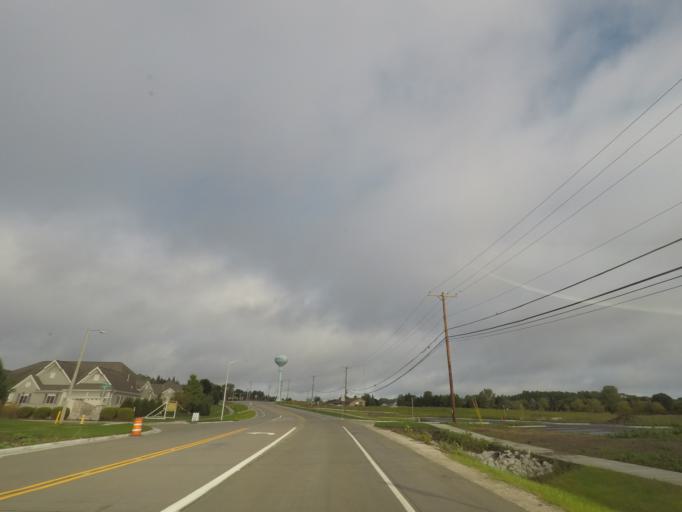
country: US
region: Wisconsin
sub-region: Waukesha County
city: Pewaukee
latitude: 43.0354
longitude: -88.2825
